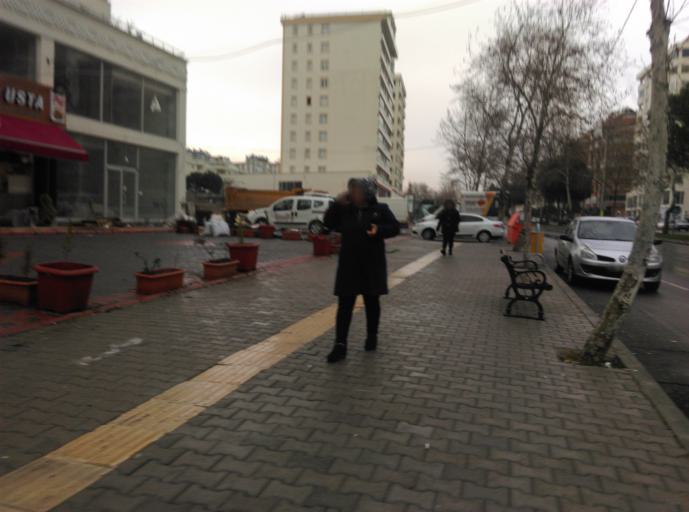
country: TR
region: Kahramanmaras
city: Kahramanmaras
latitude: 37.5845
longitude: 36.8939
